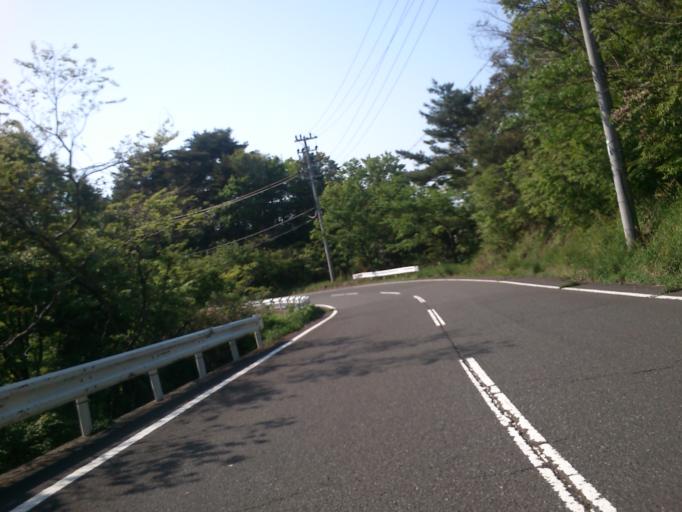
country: JP
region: Kyoto
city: Miyazu
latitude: 35.7300
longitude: 135.1831
